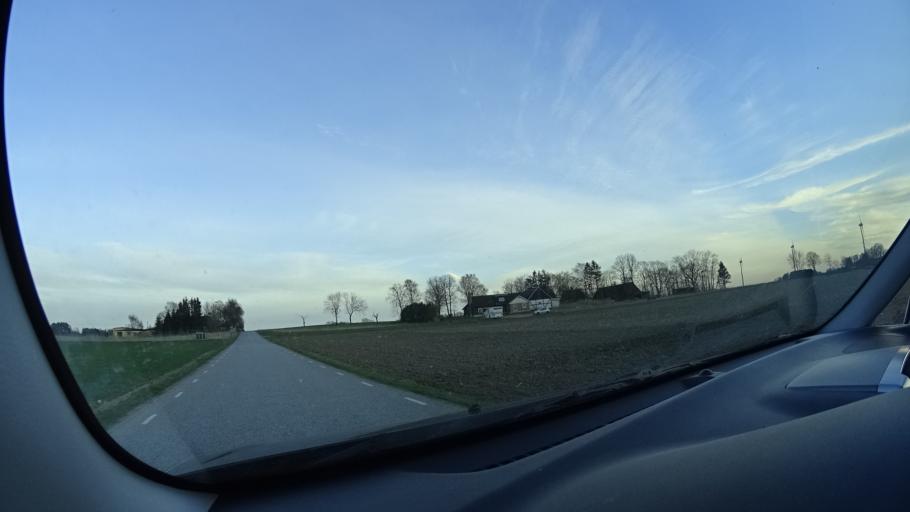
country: SE
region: Skane
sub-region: Hoors Kommun
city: Loberod
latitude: 55.8457
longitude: 13.4480
